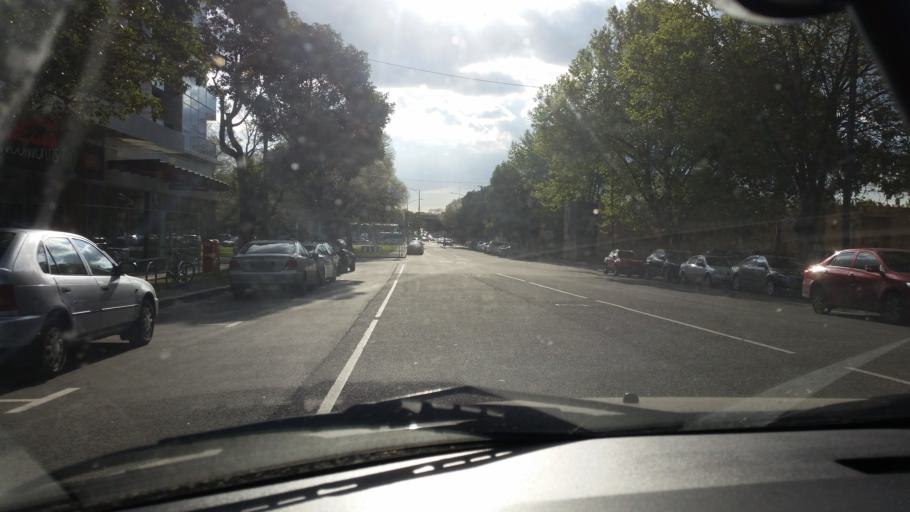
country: AU
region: Victoria
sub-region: Melbourne
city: North Melbourne
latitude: -37.7957
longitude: 144.9407
